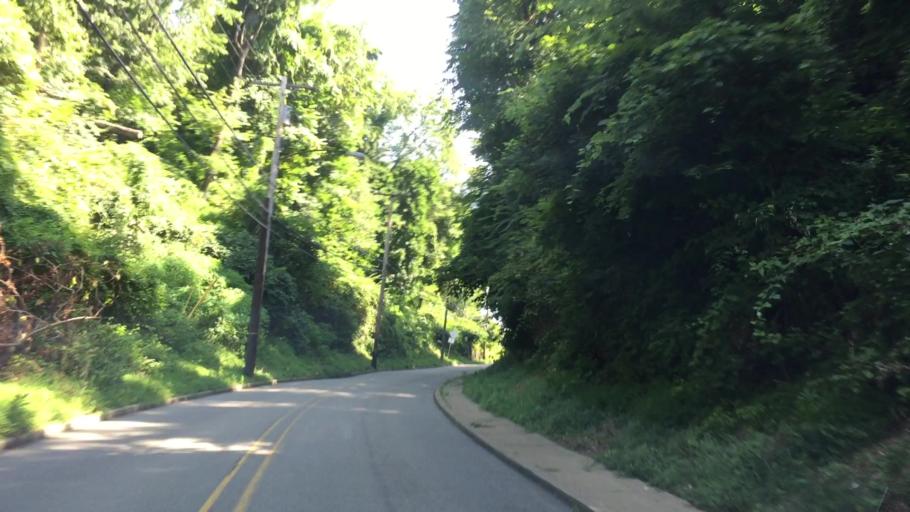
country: US
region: Pennsylvania
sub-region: Allegheny County
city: Green Tree
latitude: 40.4353
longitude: -80.0270
